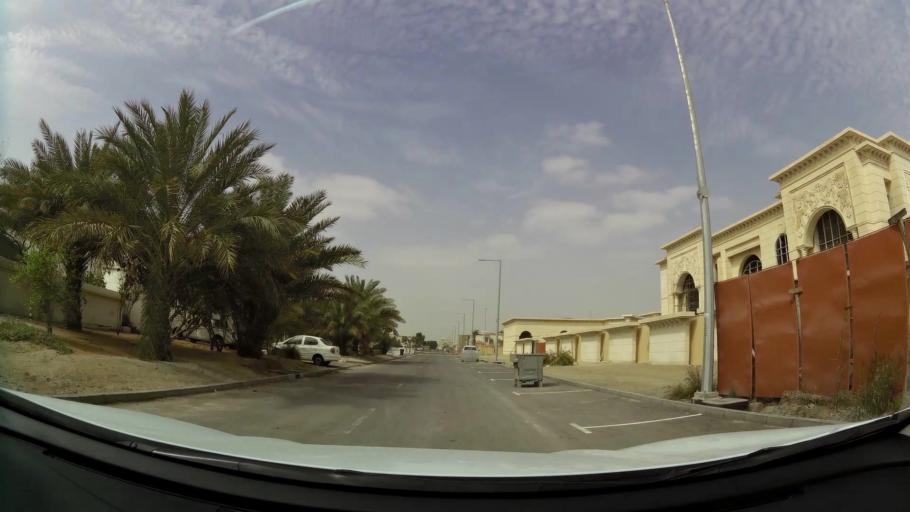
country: AE
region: Abu Dhabi
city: Abu Dhabi
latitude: 24.4004
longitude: 54.5648
